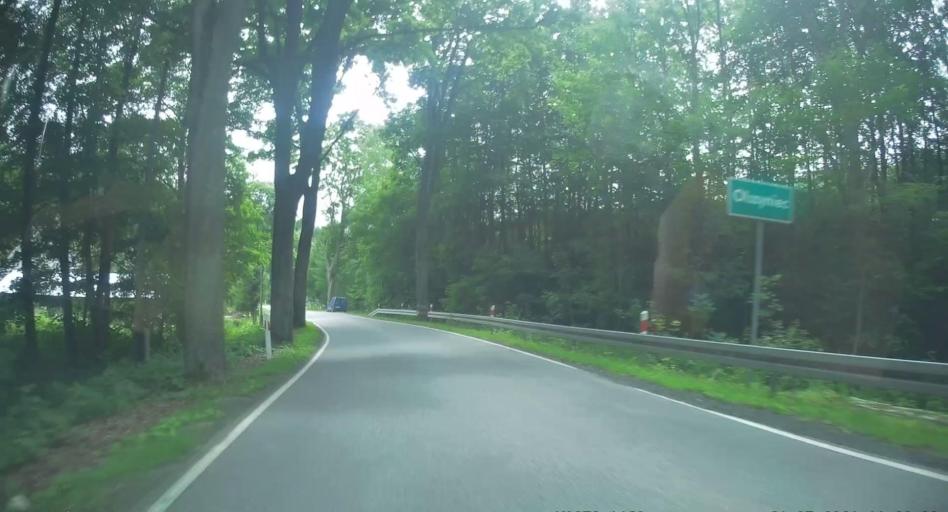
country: PL
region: Lower Silesian Voivodeship
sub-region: Powiat walbrzyski
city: Jedlina-Zdroj
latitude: 50.7308
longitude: 16.3684
